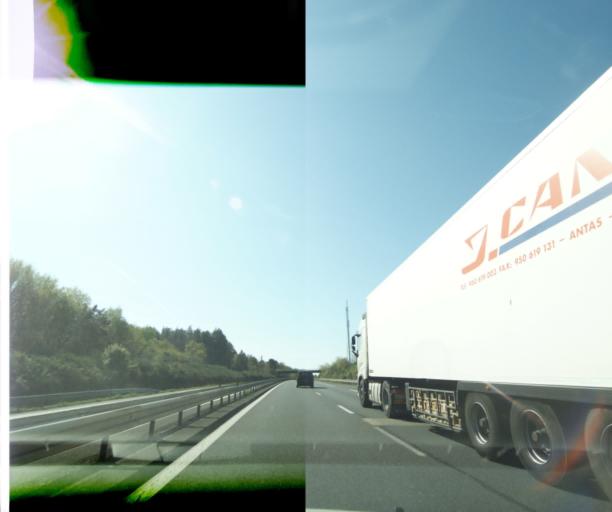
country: FR
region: Centre
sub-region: Departement du Loiret
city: La Ferte-Saint-Aubin
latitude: 47.7053
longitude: 1.9020
